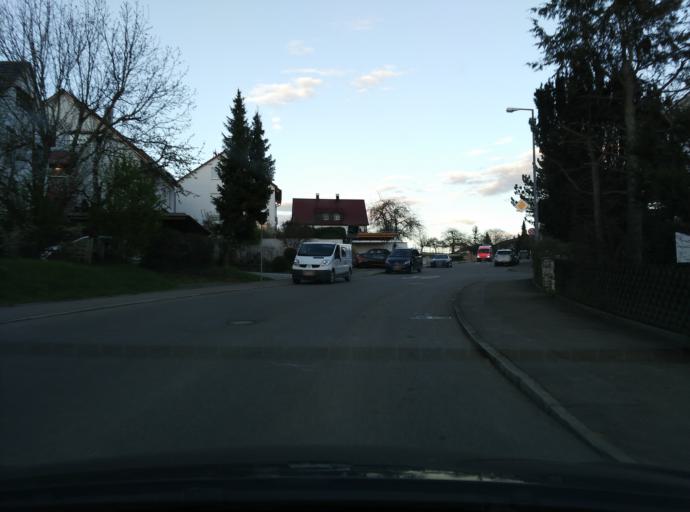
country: DE
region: Baden-Wuerttemberg
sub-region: Regierungsbezirk Stuttgart
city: Nurtingen
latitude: 48.6315
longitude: 9.3474
